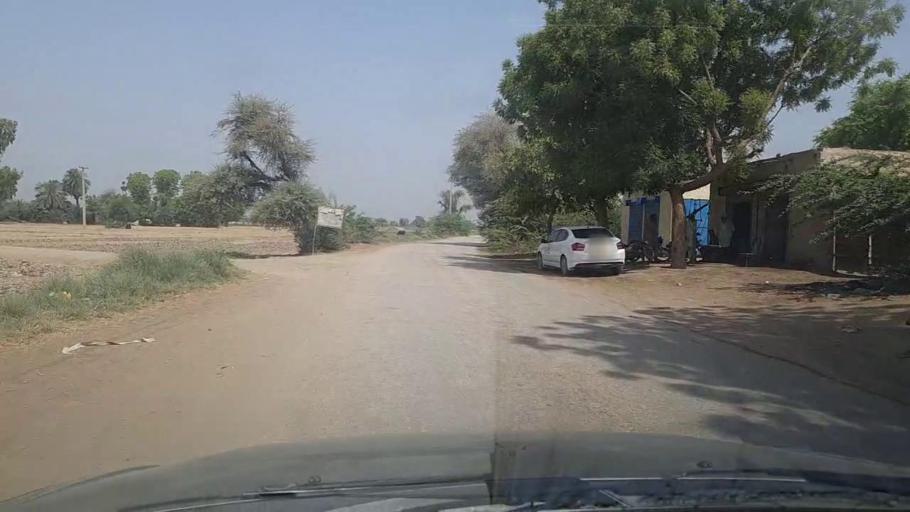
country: PK
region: Sindh
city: Setharja Old
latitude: 27.1336
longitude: 68.5309
